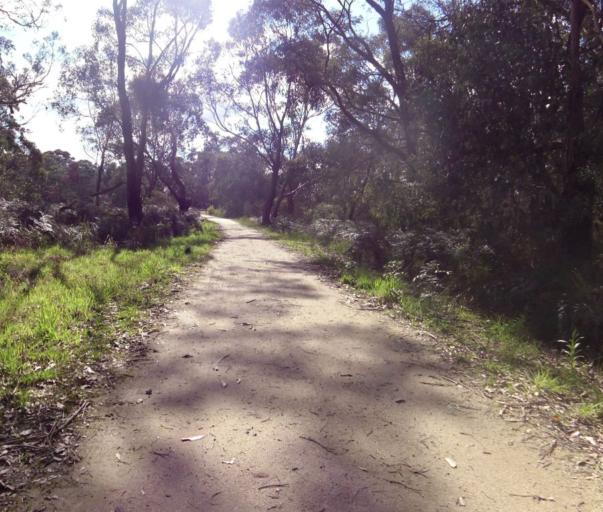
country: AU
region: Victoria
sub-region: Baw Baw
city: Warragul
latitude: -38.5778
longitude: 146.0305
